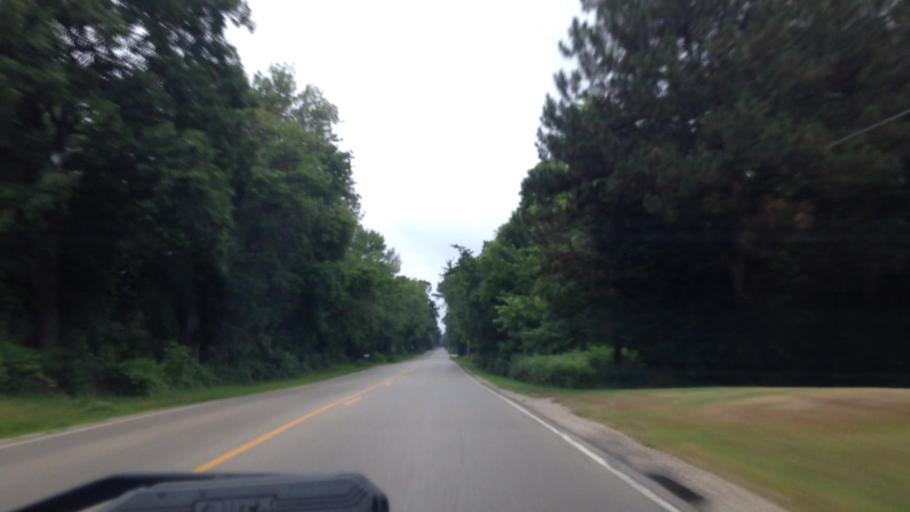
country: US
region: Wisconsin
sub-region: Waukesha County
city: Lannon
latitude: 43.1701
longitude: -88.1831
